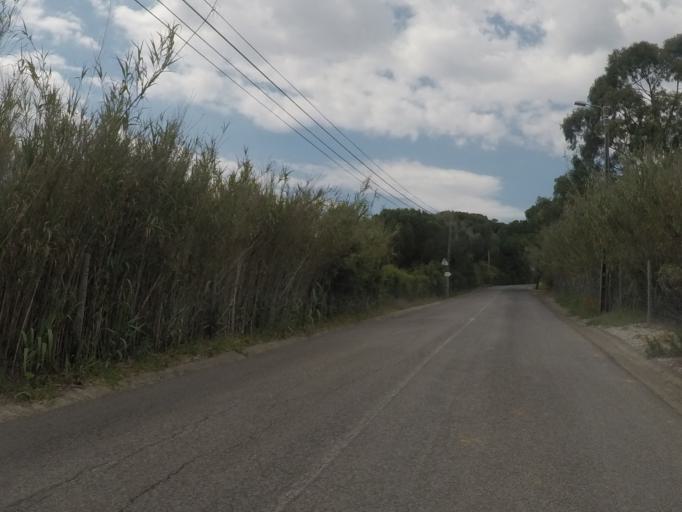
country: PT
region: Setubal
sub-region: Palmela
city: Quinta do Anjo
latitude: 38.5071
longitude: -9.0010
